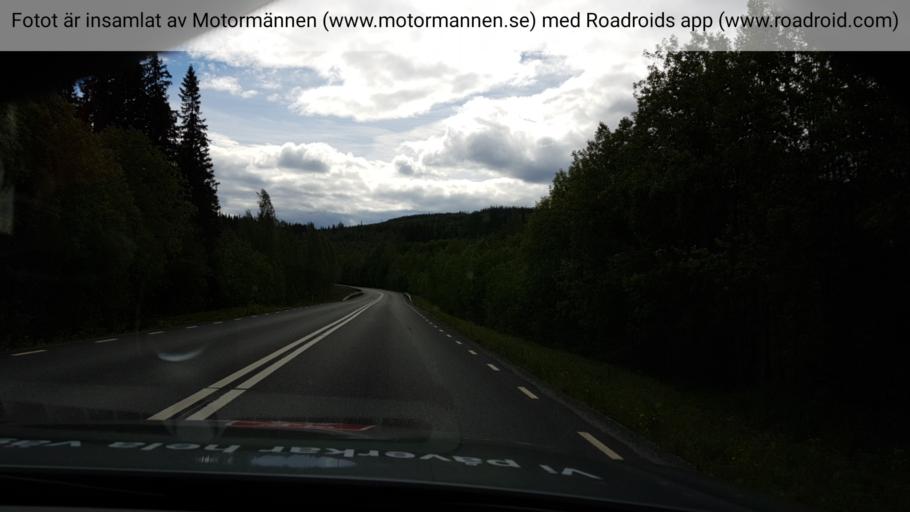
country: SE
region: Jaemtland
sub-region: Stroemsunds Kommun
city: Stroemsund
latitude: 64.0954
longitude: 15.5761
